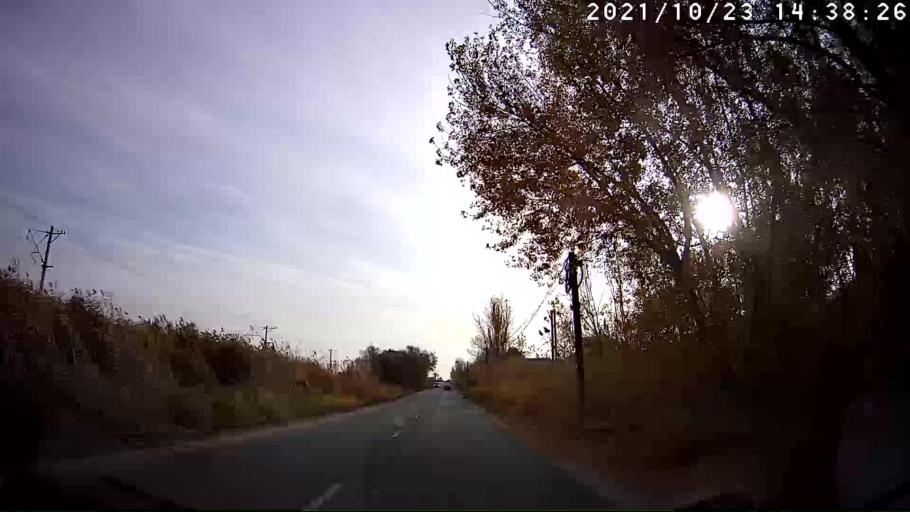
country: RU
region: Volgograd
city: Krasnoslobodsk
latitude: 48.4919
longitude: 44.5492
